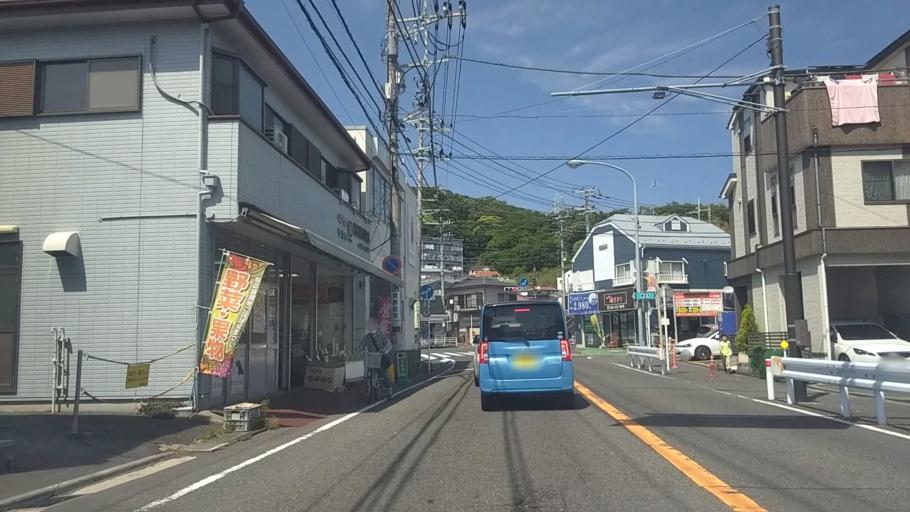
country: JP
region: Kanagawa
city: Zushi
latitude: 35.3275
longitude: 139.6143
